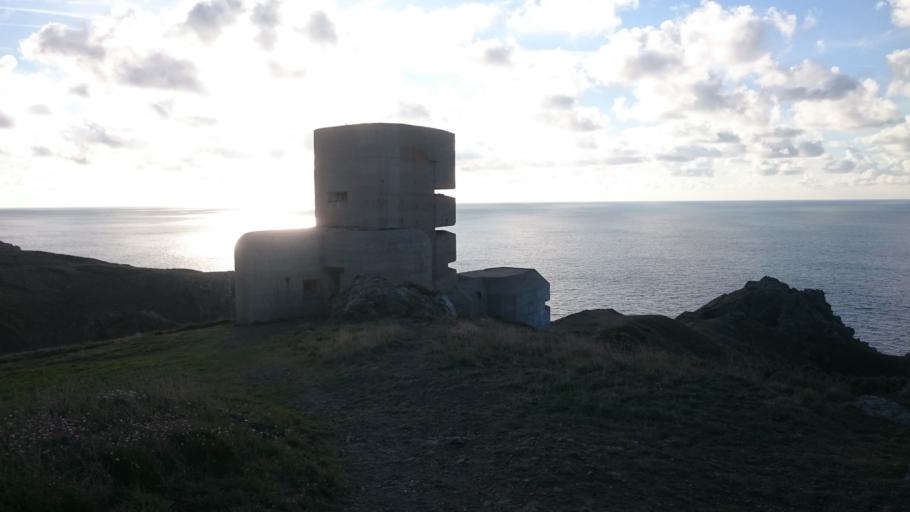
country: GG
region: St Peter Port
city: Saint Peter Port
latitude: 49.4255
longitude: -2.6641
